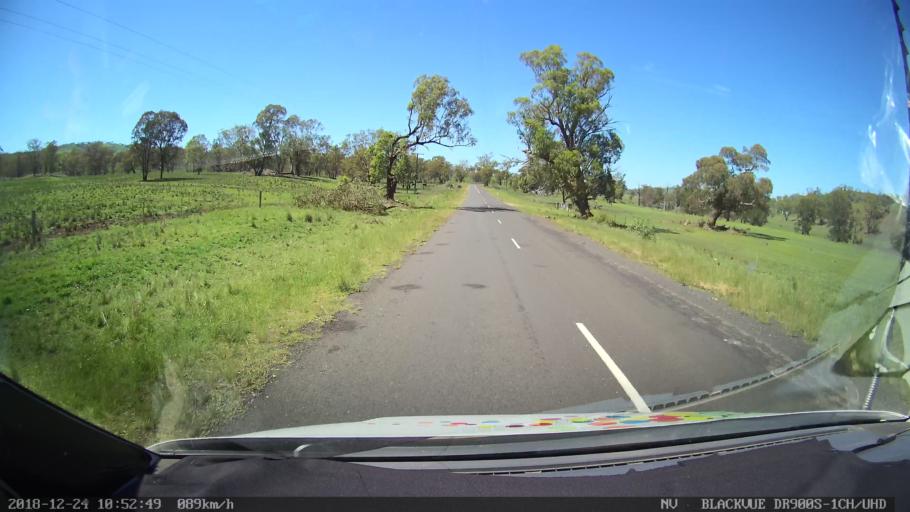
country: AU
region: New South Wales
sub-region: Upper Hunter Shire
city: Merriwa
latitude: -31.9849
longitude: 150.4226
